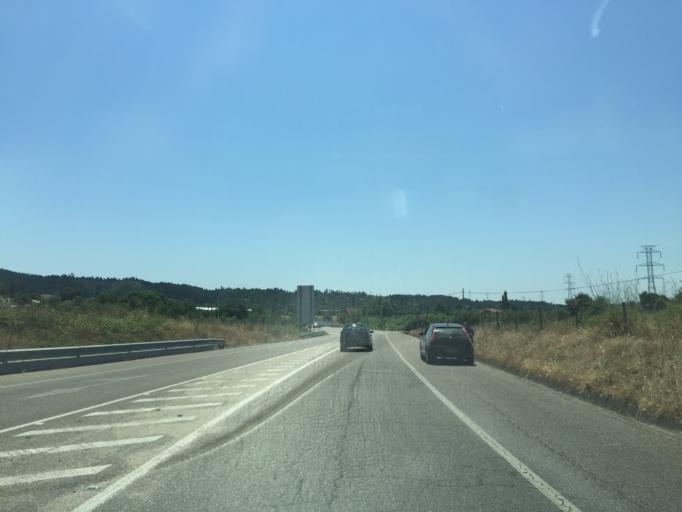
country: PT
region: Santarem
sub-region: Tomar
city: Tomar
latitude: 39.5935
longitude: -8.3614
